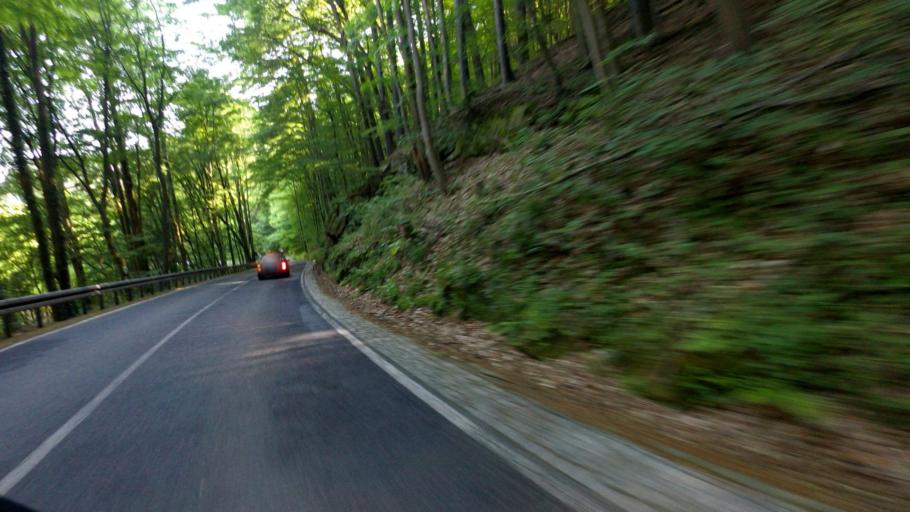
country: DE
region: Saxony
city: Hohnstein
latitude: 50.9830
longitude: 14.1051
